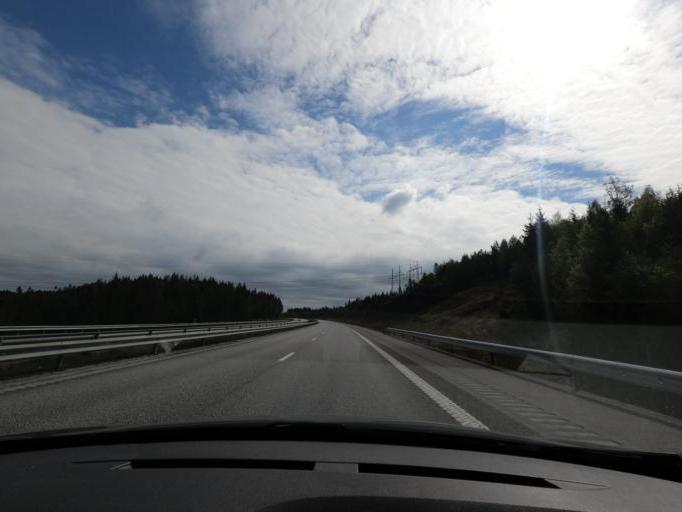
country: SE
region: Vaestra Goetaland
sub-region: Harryda Kommun
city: Hindas
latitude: 57.6666
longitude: 12.4038
